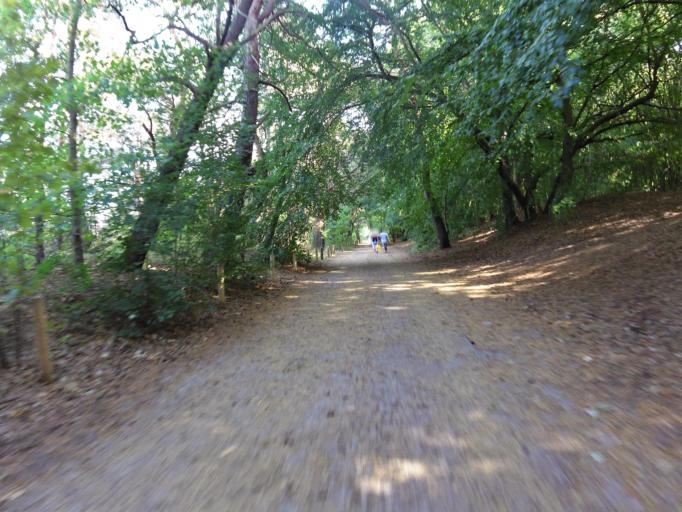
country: DE
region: Mecklenburg-Vorpommern
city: Ostseebad Zinnowitz
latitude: 54.0782
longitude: 13.9235
